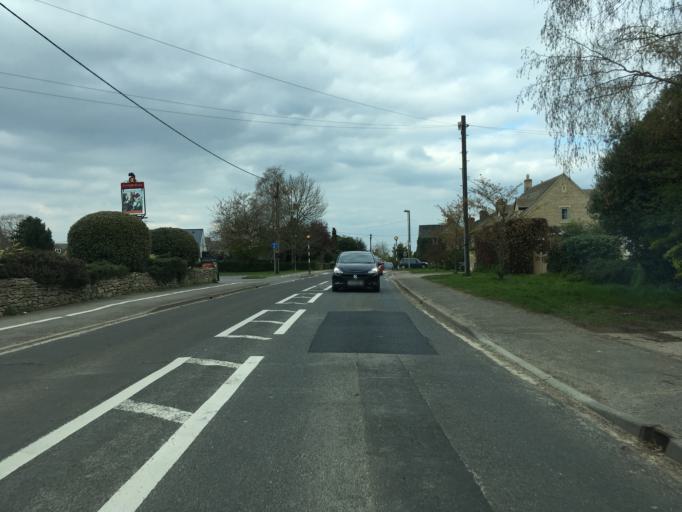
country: GB
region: England
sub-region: Oxfordshire
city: Woodstock
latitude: 51.8256
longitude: -1.3825
